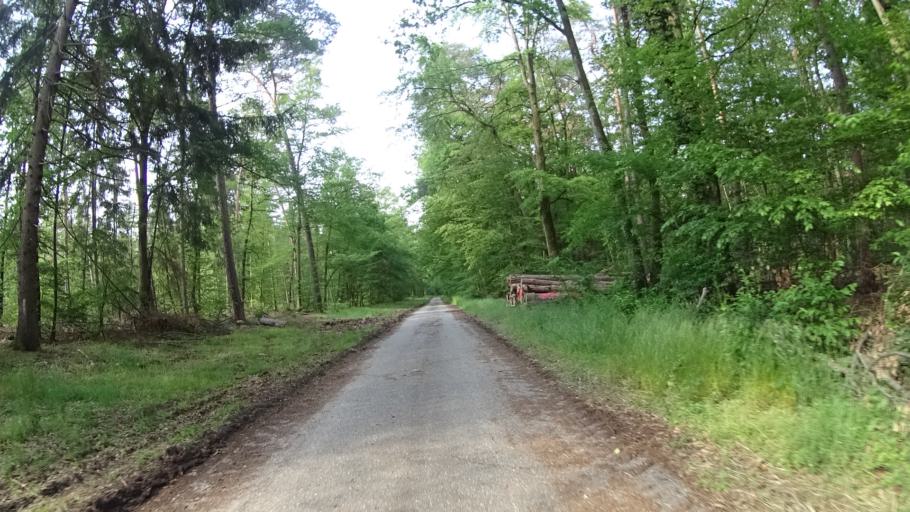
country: DE
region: Baden-Wuerttemberg
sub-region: Karlsruhe Region
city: Sandhausen
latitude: 49.3403
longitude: 8.6284
